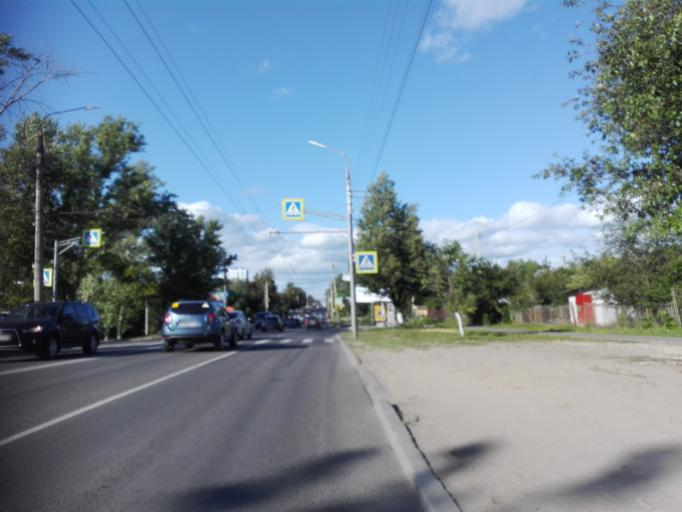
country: RU
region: Orjol
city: Orel
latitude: 52.9944
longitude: 36.1296
